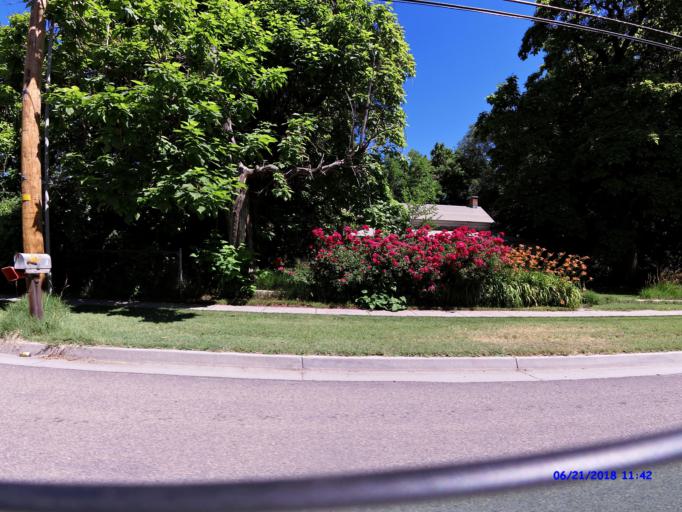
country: US
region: Utah
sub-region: Weber County
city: Harrisville
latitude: 41.2594
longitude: -111.9797
